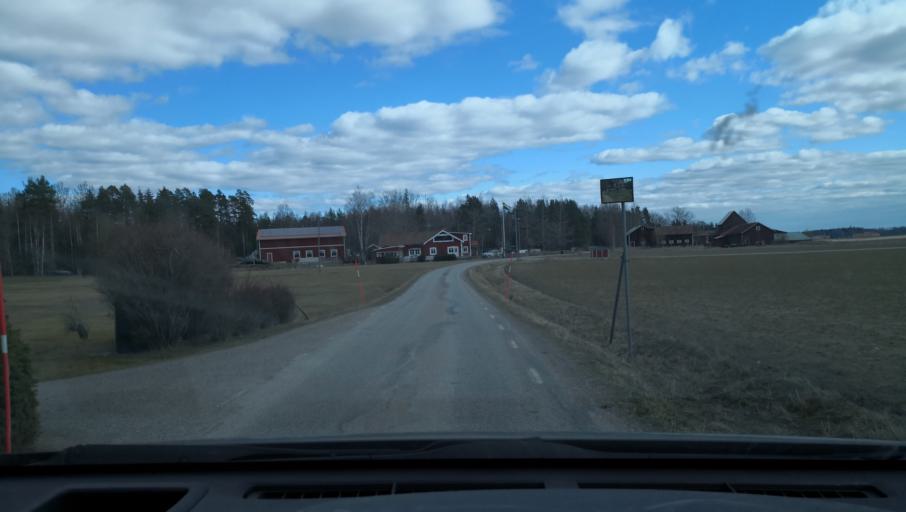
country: SE
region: Vaestmanland
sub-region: Sala Kommun
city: Sala
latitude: 59.8619
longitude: 16.5950
